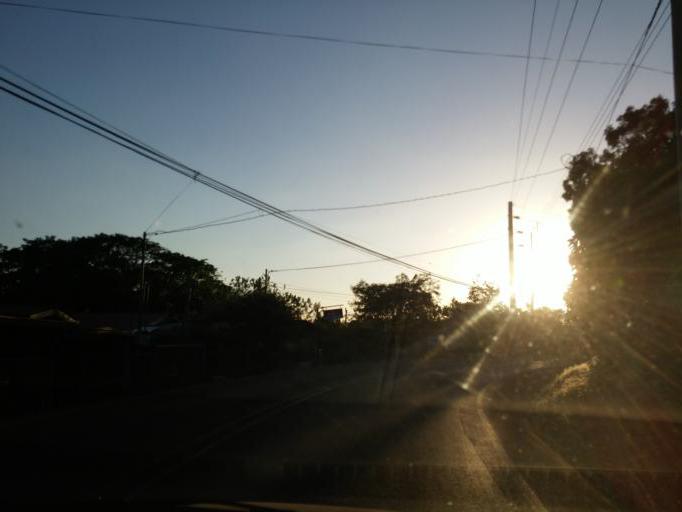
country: CR
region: Alajuela
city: Orotina
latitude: 9.9146
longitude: -84.5323
